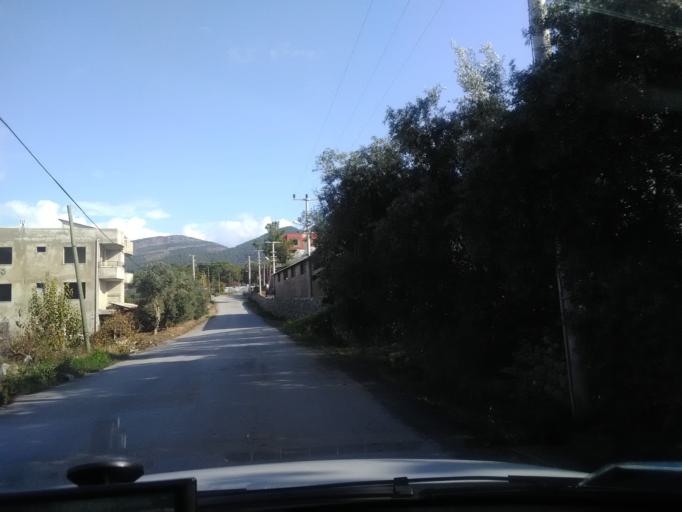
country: TR
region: Antalya
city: Gazipasa
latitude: 36.2878
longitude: 32.3206
